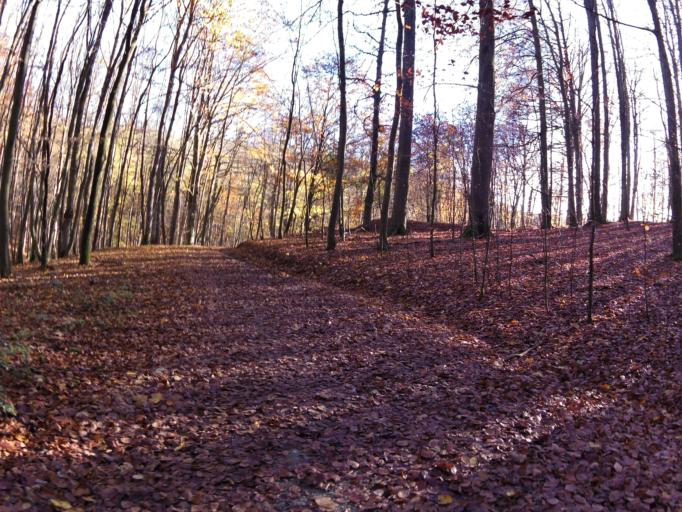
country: DE
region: Thuringia
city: Kammerforst
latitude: 51.0717
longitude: 10.4360
